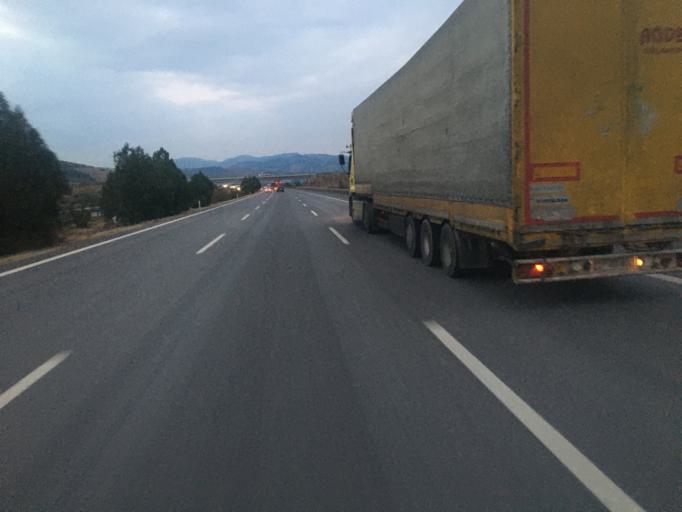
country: TR
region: Osmaniye
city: Osmaniye
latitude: 37.1460
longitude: 36.3340
